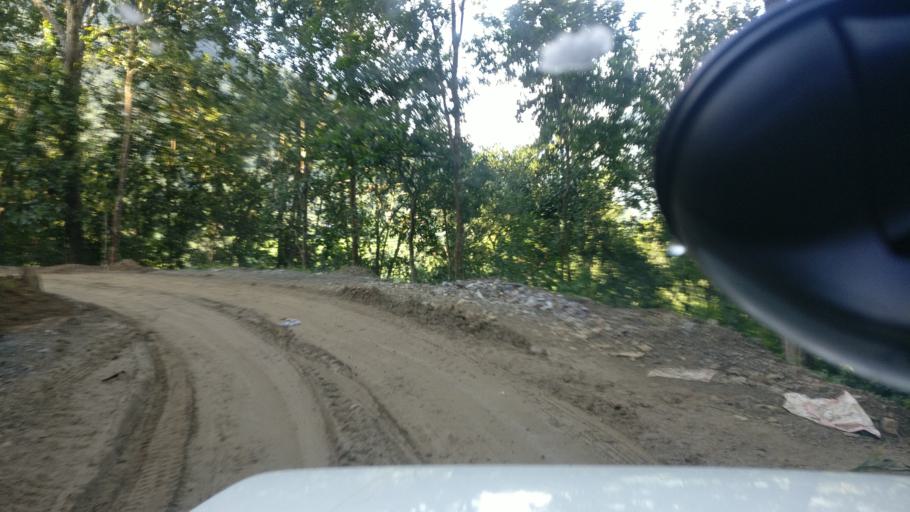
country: NP
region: Western Region
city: Baglung
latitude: 28.1491
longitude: 83.6580
